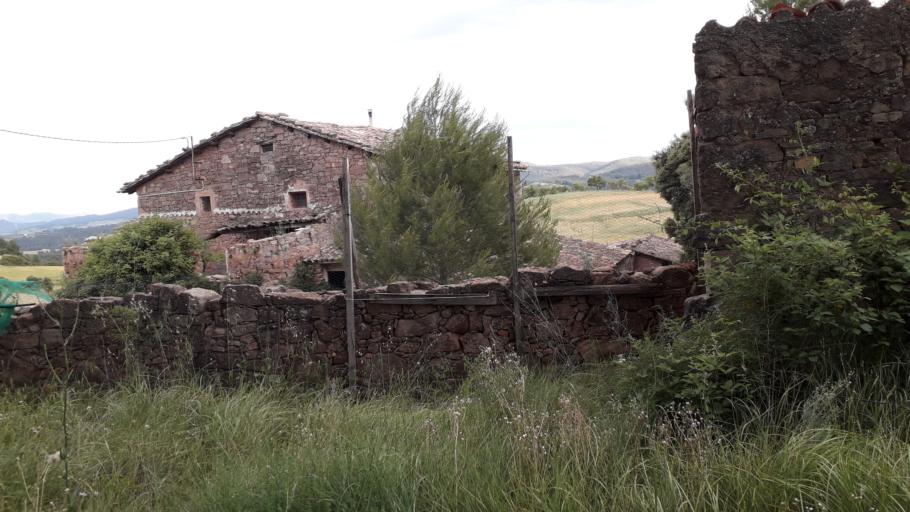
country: ES
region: Catalonia
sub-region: Provincia de Barcelona
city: Jorba
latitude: 41.5861
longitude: 1.5402
